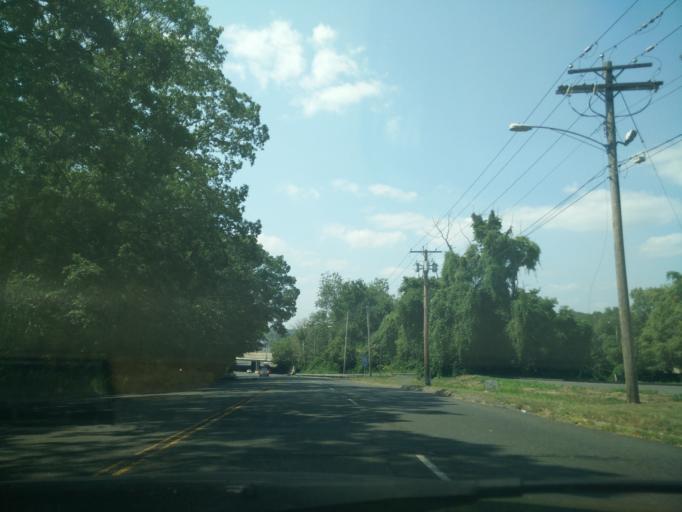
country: US
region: Connecticut
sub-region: Fairfield County
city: Southport
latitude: 41.1396
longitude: -73.2845
